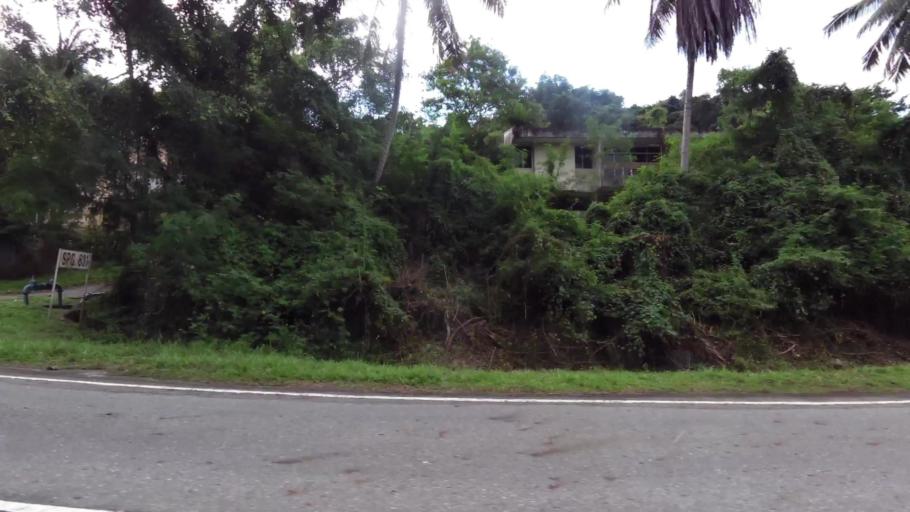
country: BN
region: Brunei and Muara
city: Bandar Seri Begawan
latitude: 4.9082
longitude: 114.9971
